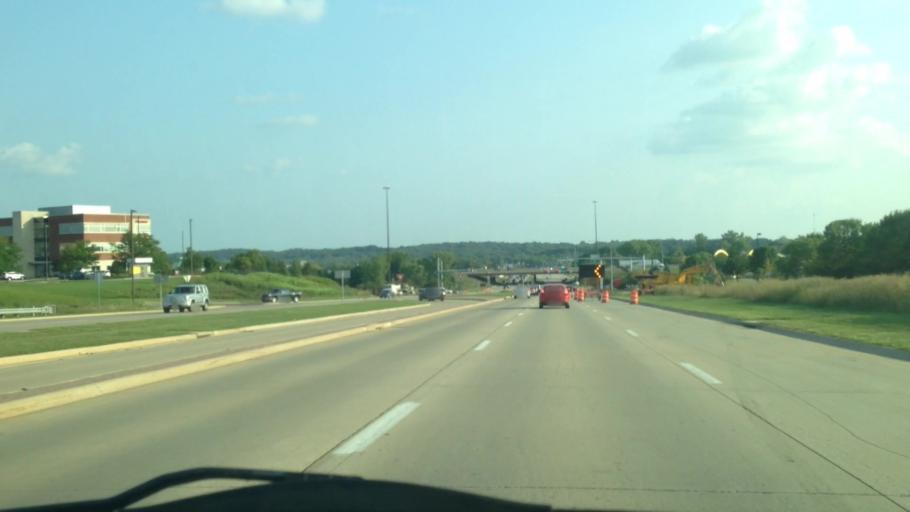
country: US
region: Iowa
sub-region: Johnson County
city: Coralville
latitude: 41.6986
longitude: -91.6086
